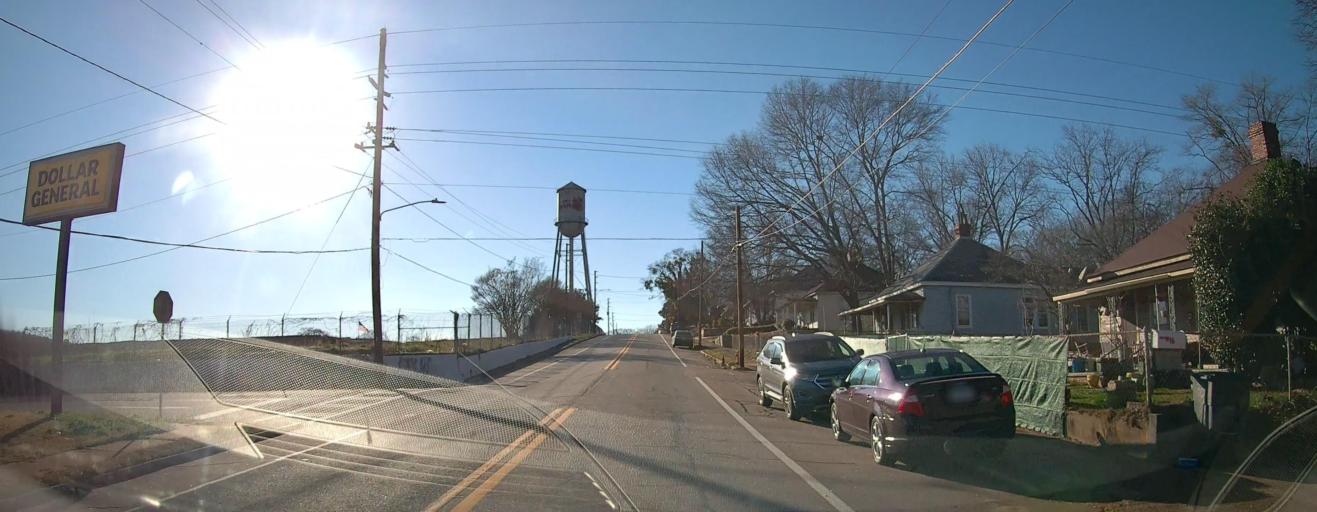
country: US
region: Georgia
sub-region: Meriwether County
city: Manchester
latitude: 32.8569
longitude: -84.6063
